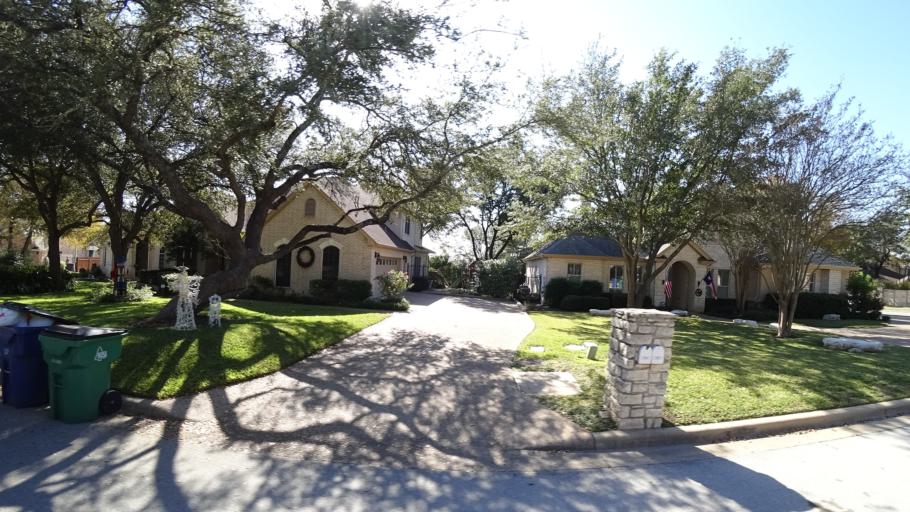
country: US
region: Texas
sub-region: Travis County
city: Lost Creek
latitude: 30.3712
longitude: -97.8450
